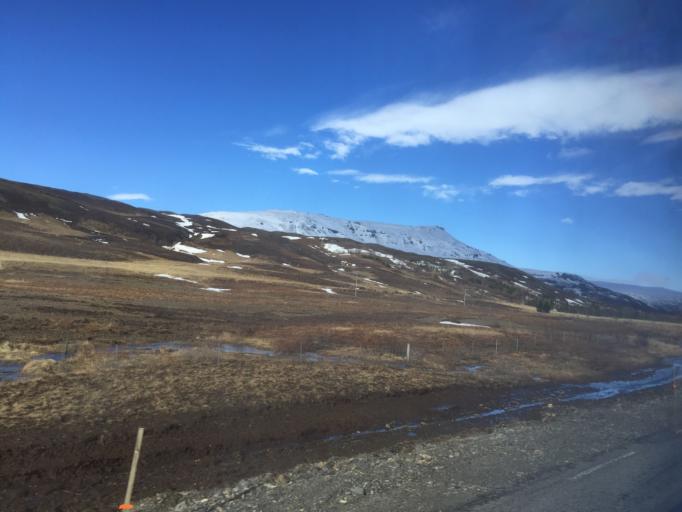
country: IS
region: South
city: Selfoss
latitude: 64.2767
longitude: -20.3498
